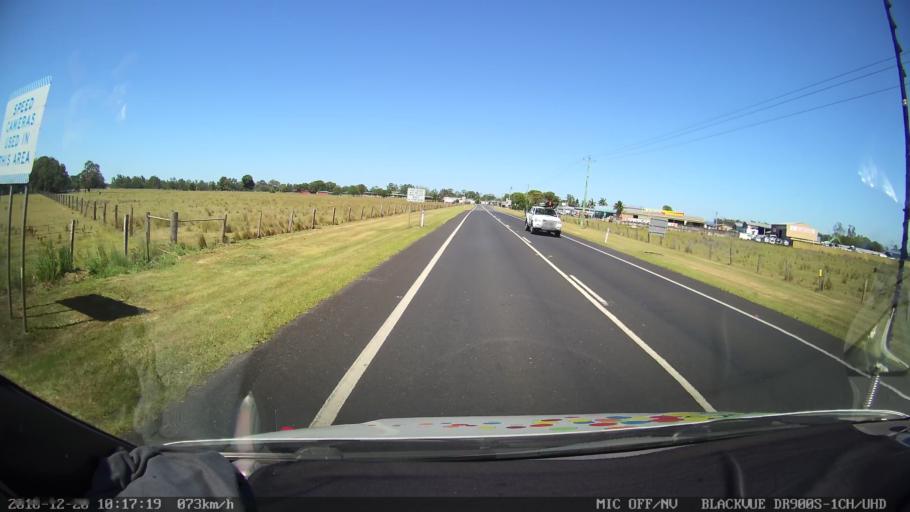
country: AU
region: New South Wales
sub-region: Richmond Valley
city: Casino
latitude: -28.8602
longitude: 153.0720
